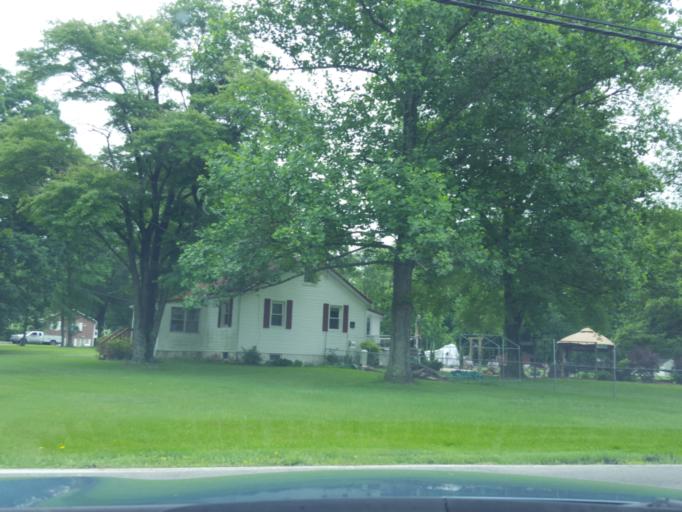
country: US
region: Maryland
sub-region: Prince George's County
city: Marlboro Meadows
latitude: 38.7956
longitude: -76.6869
